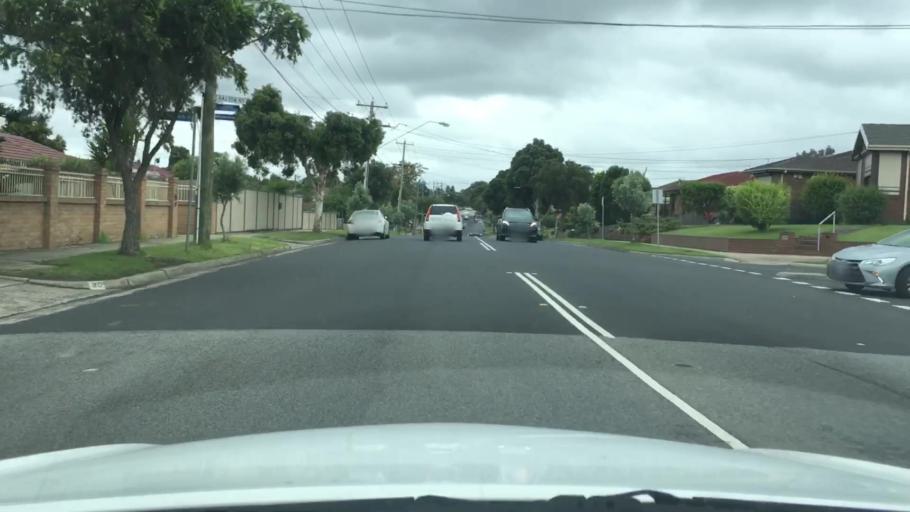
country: AU
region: Victoria
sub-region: Greater Dandenong
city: Noble Park North
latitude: -37.9548
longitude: 145.1907
